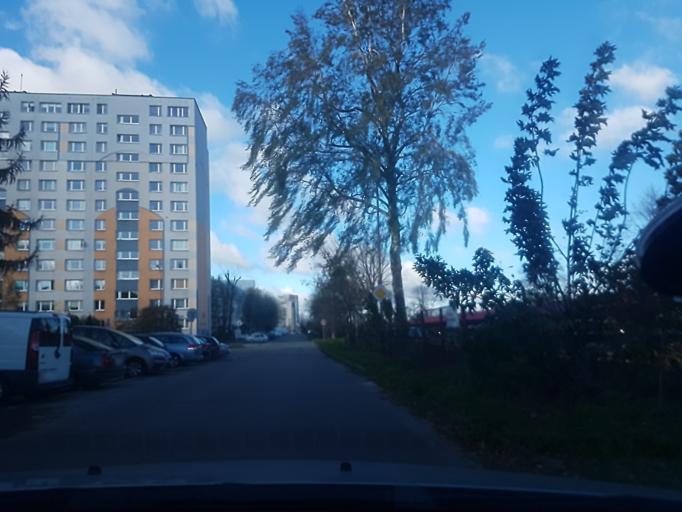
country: PL
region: Lodz Voivodeship
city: Lodz
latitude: 51.7612
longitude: 19.5315
